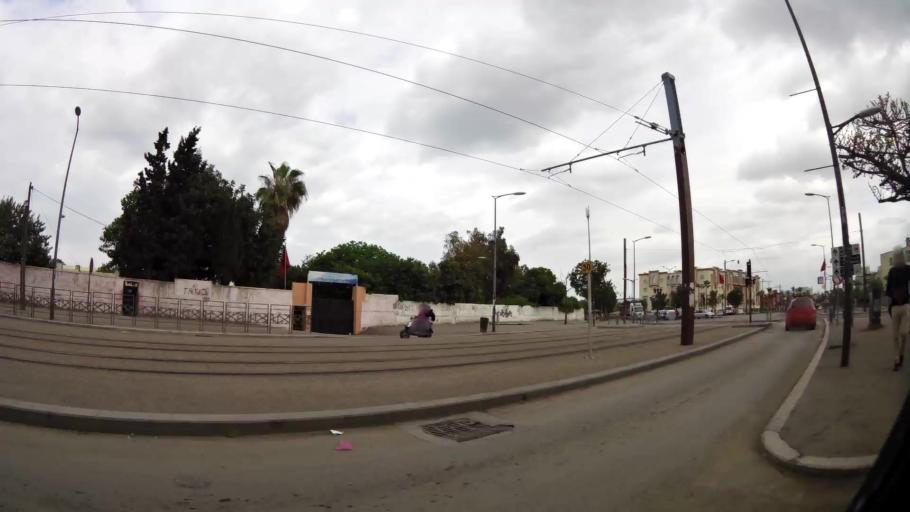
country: MA
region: Grand Casablanca
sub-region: Casablanca
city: Casablanca
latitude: 33.5906
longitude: -7.5725
